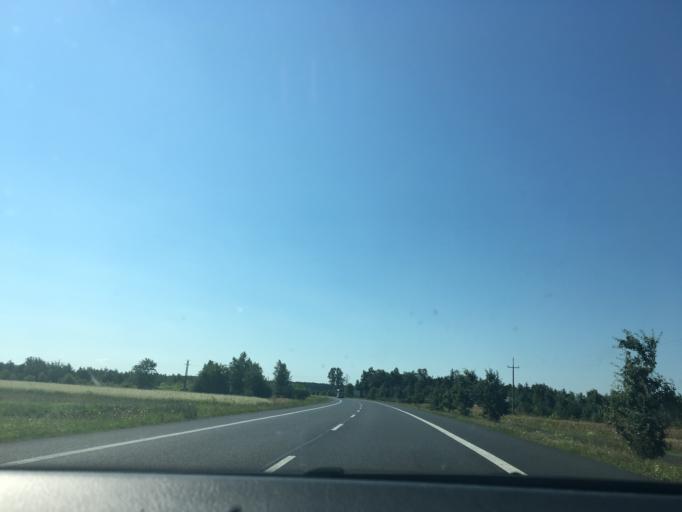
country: PL
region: Lublin Voivodeship
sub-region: Powiat lubartowski
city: Lubartow
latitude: 51.4571
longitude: 22.5757
